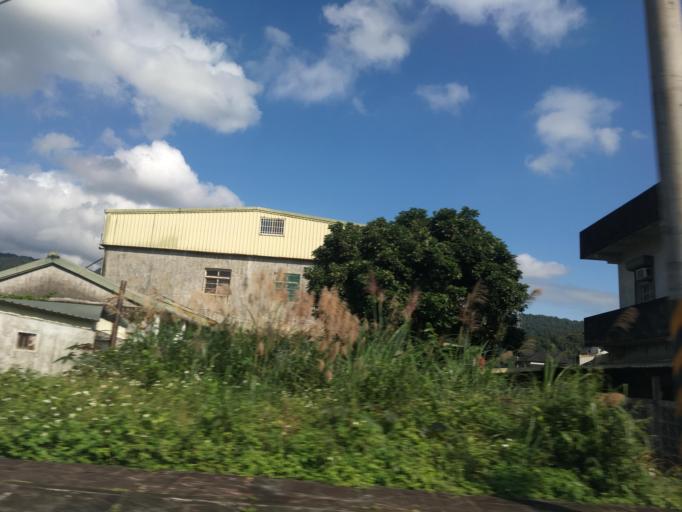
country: TW
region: Taiwan
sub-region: Yilan
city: Yilan
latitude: 24.7457
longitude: 121.6962
